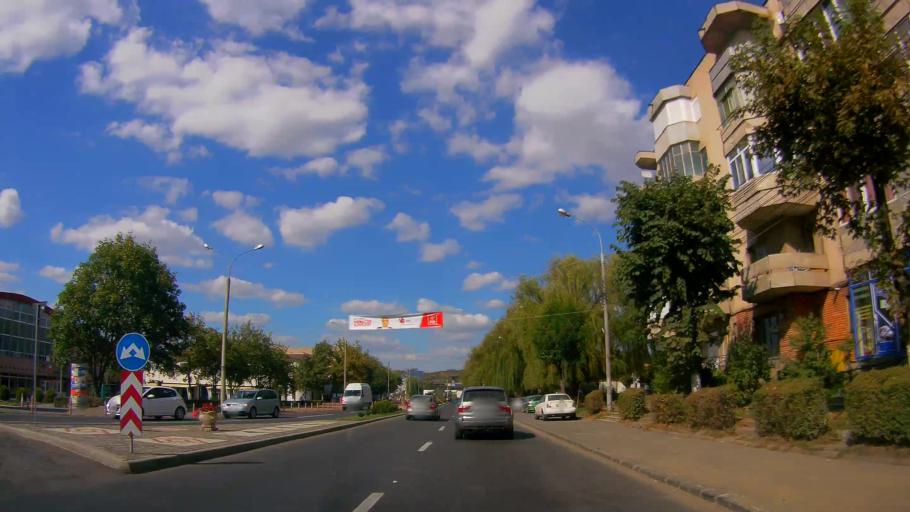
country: RO
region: Salaj
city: Zalau
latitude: 47.1954
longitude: 23.0605
